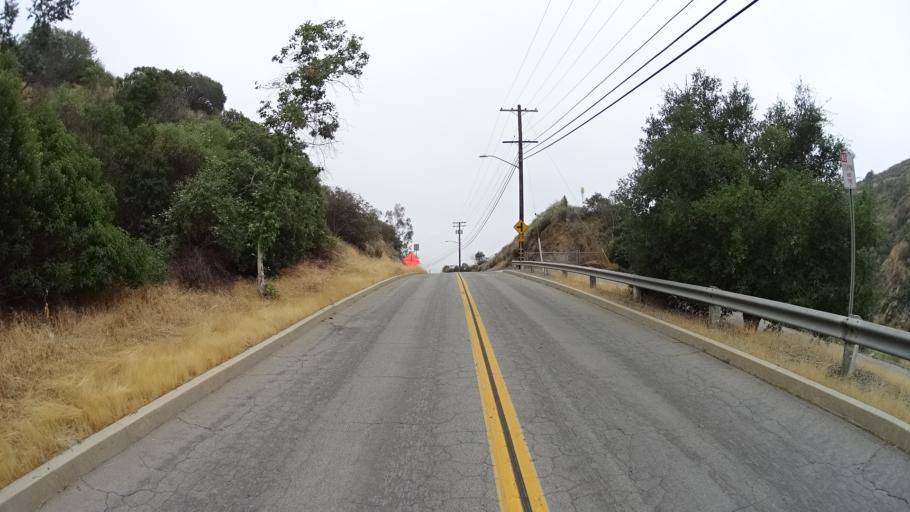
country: US
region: California
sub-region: Los Angeles County
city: Burbank
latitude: 34.1974
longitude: -118.2956
